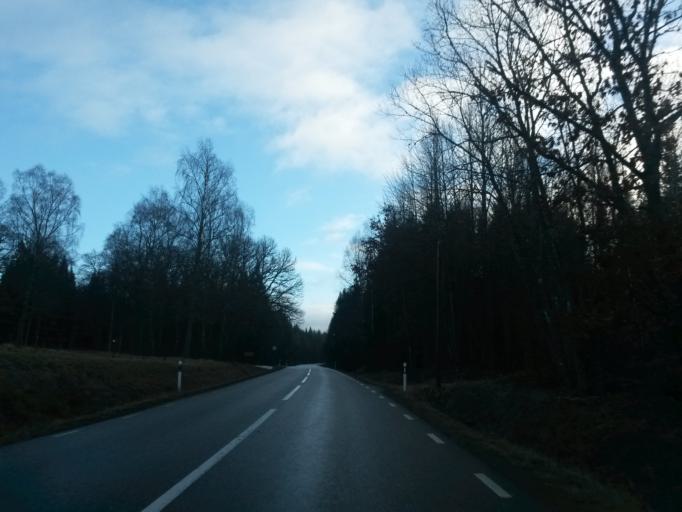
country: SE
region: Vaestra Goetaland
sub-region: Boras Kommun
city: Boras
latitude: 57.8439
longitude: 12.9634
